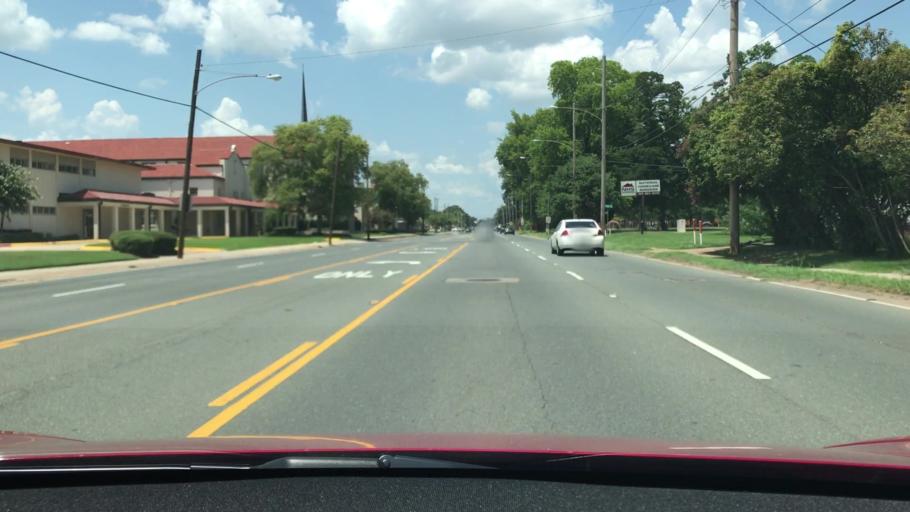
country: US
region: Louisiana
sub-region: Bossier Parish
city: Bossier City
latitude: 32.4628
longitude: -93.7221
